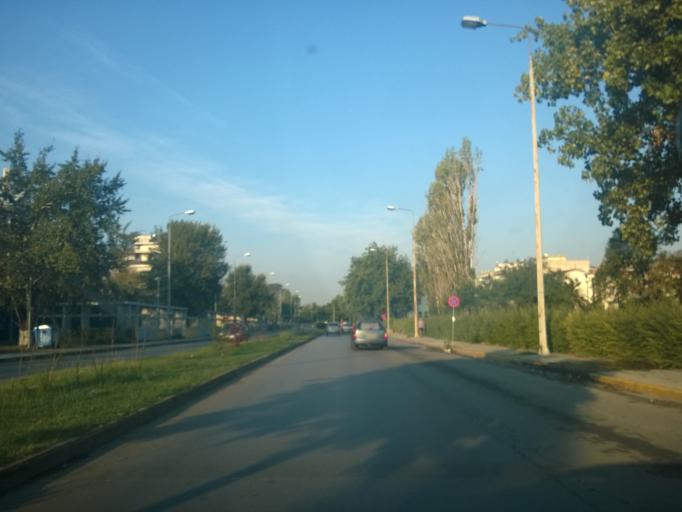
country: GR
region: Central Macedonia
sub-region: Nomos Thessalonikis
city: Evosmos
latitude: 40.6603
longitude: 22.9106
